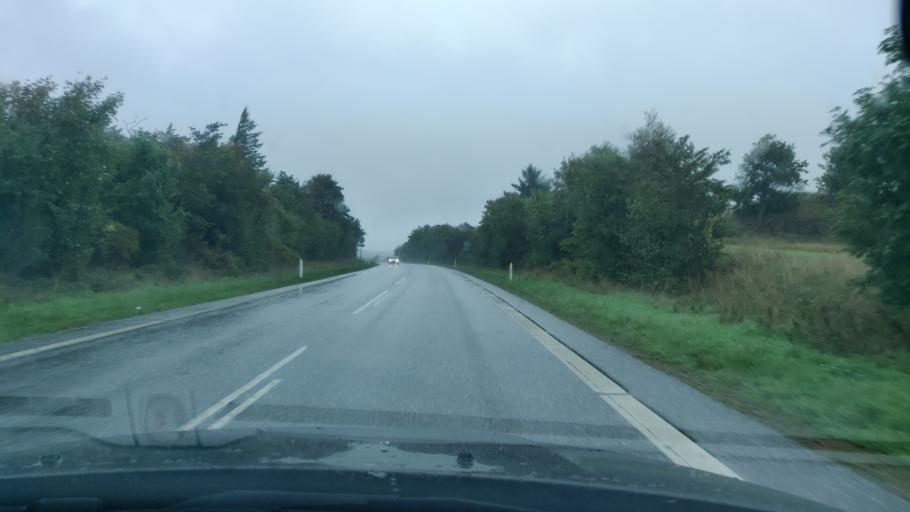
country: DK
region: North Denmark
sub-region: Thisted Kommune
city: Hurup
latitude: 56.8463
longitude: 8.5346
